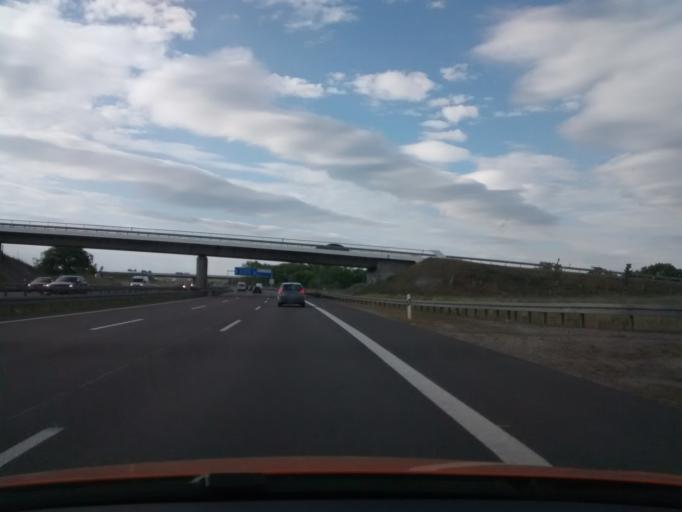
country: DE
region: Brandenburg
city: Schulzendorf
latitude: 52.3683
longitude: 13.5486
